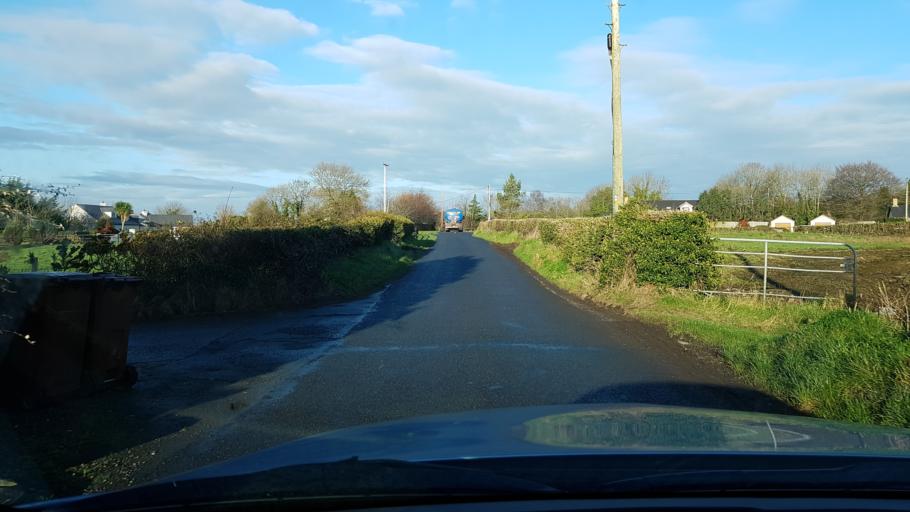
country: GB
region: Northern Ireland
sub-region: Ards District
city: Greyabbey
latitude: 54.5563
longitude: -5.5477
